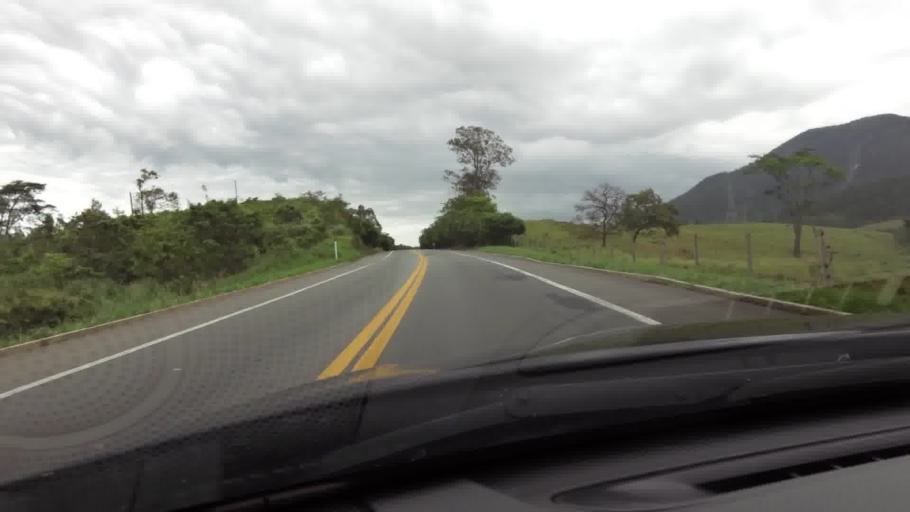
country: BR
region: Espirito Santo
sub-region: Guarapari
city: Guarapari
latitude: -20.6235
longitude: -40.5232
